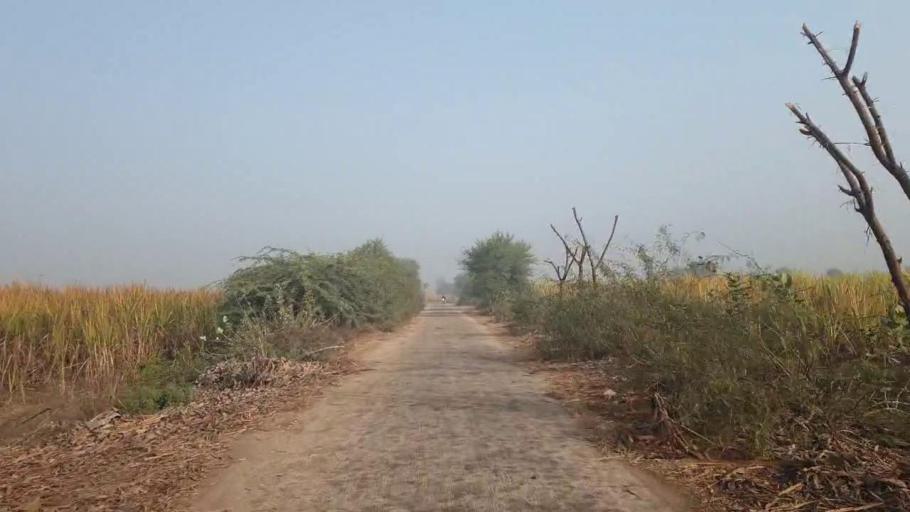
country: PK
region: Sindh
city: Tando Adam
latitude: 25.8157
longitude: 68.6323
